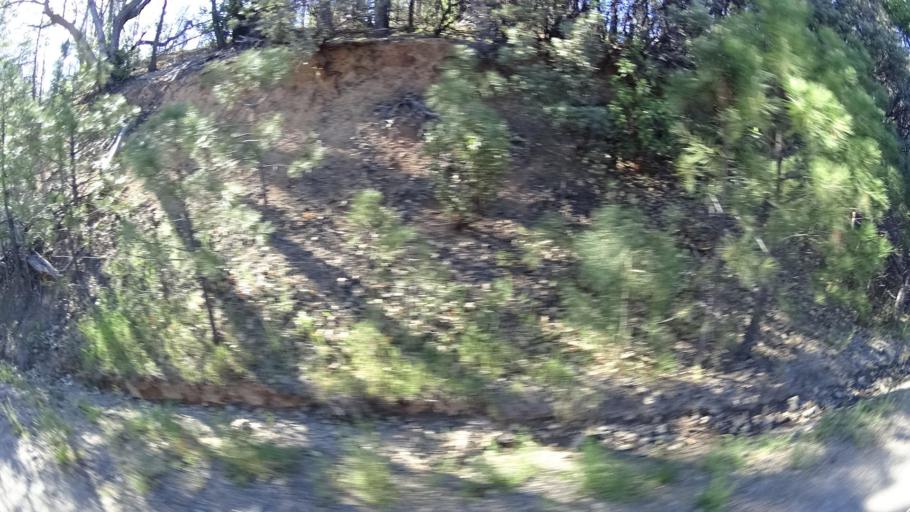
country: US
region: California
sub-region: Lake County
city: Upper Lake
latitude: 39.3948
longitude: -122.9729
